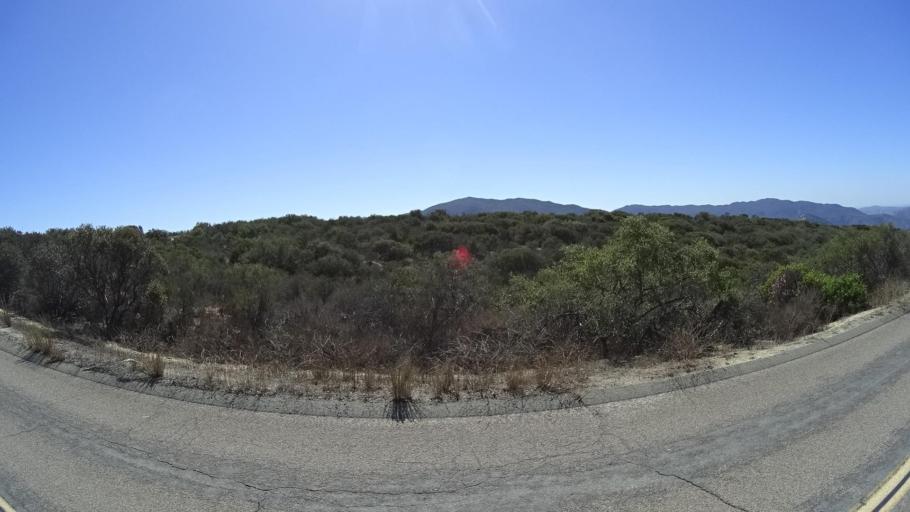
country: US
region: California
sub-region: San Diego County
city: Harbison Canyon
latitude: 32.7960
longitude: -116.7958
